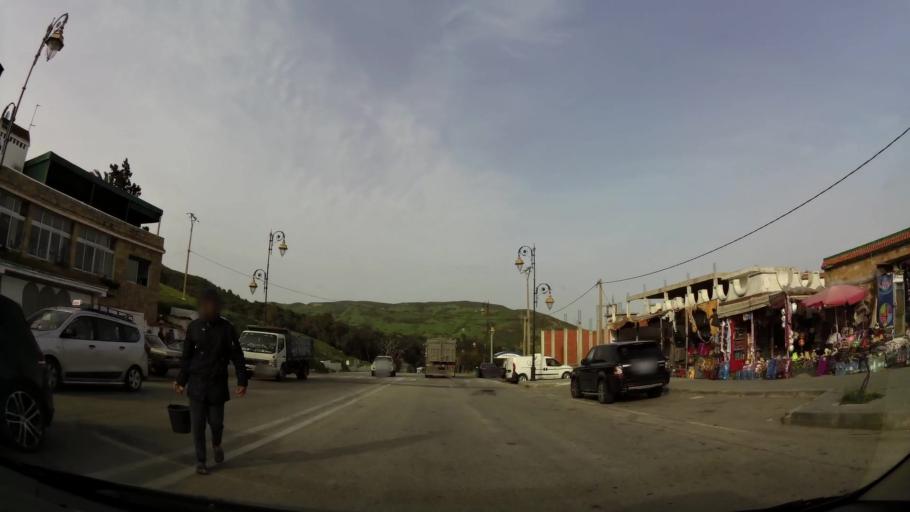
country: MA
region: Tanger-Tetouan
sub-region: Tetouan
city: Saddina
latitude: 35.5481
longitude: -5.5549
